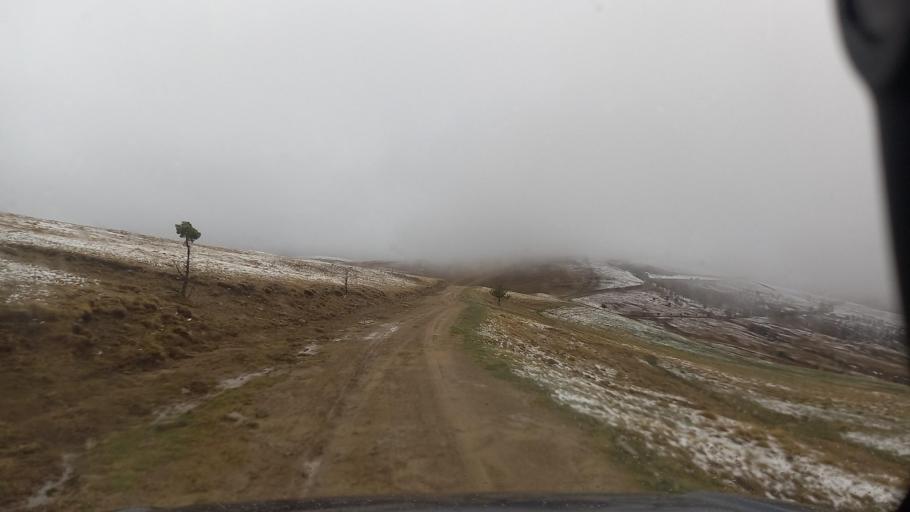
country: RU
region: Karachayevo-Cherkesiya
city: Uchkeken
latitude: 43.6019
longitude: 42.5588
